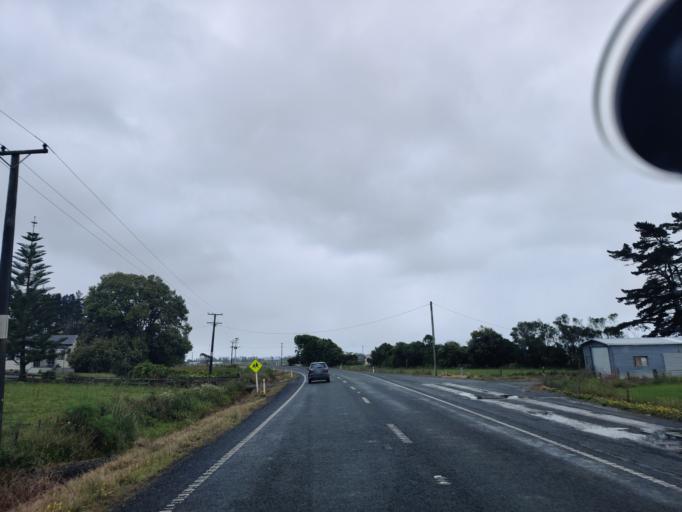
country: NZ
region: Northland
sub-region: Kaipara District
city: Dargaville
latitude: -35.9948
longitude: 173.9195
